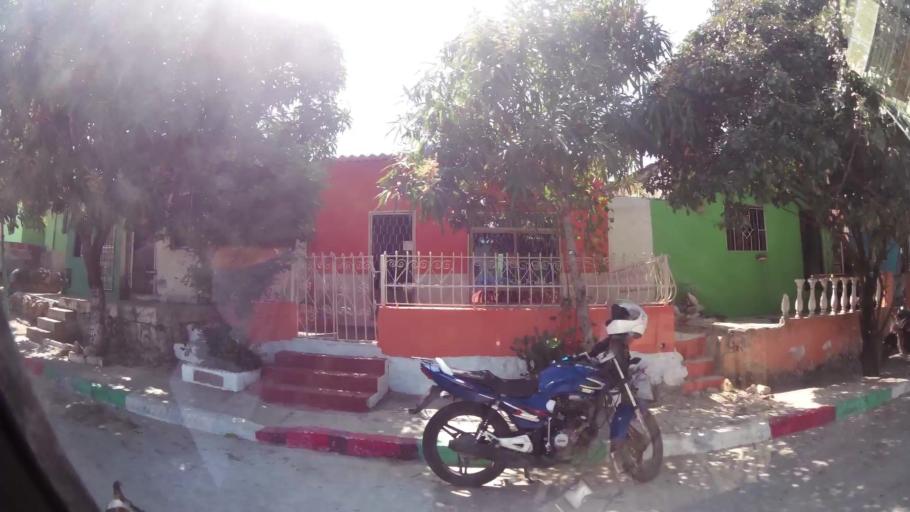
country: CO
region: Atlantico
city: Barranquilla
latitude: 10.9619
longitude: -74.8240
